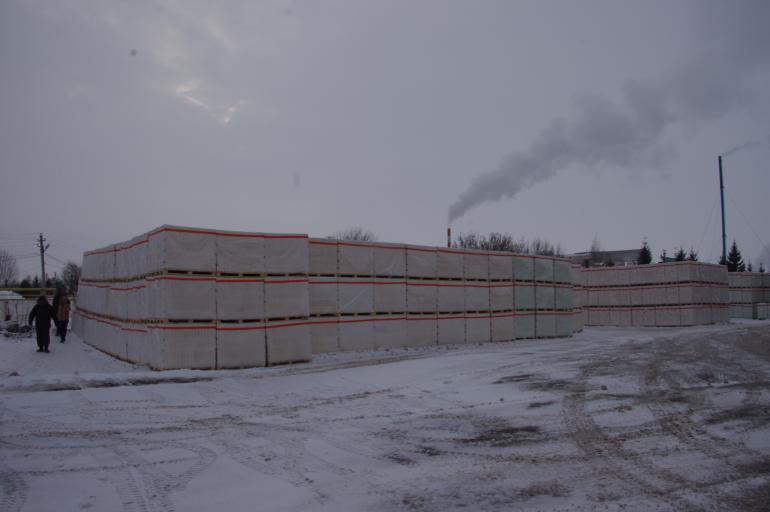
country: RU
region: Nizjnij Novgorod
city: Arzamas
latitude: 55.2984
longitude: 43.9301
